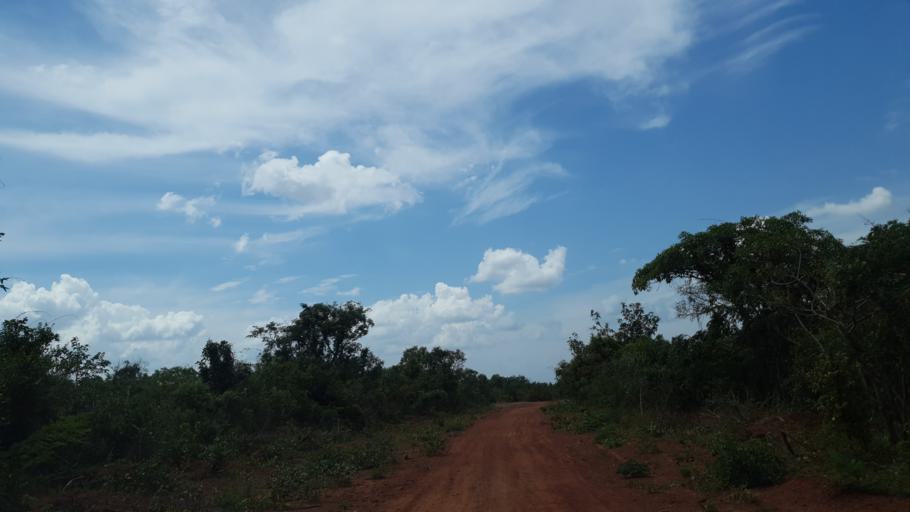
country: ML
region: Sikasso
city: Sikasso
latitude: 11.6862
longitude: -6.2156
